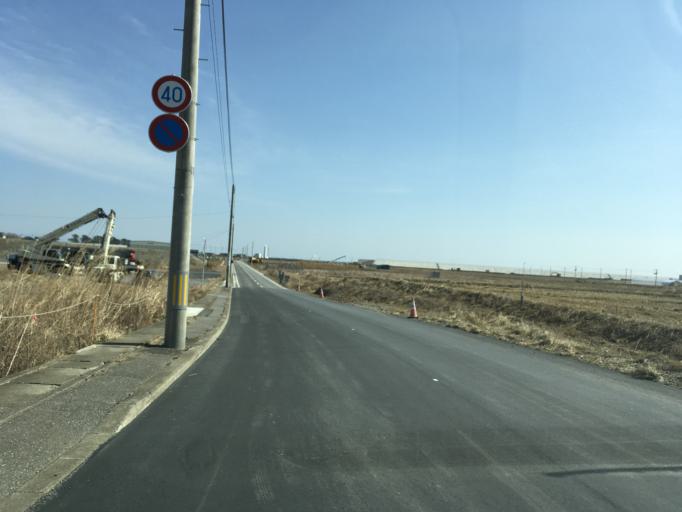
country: JP
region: Iwate
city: Ofunato
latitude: 38.8306
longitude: 141.5873
